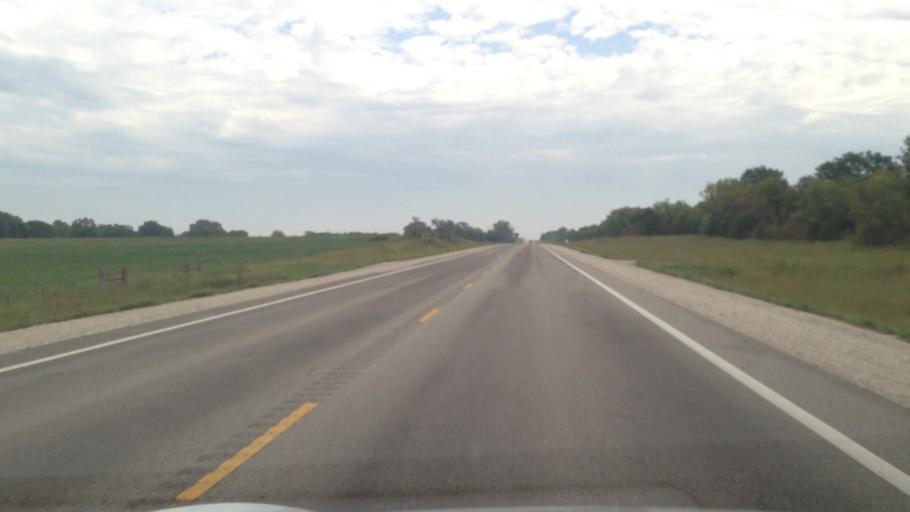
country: US
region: Kansas
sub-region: Allen County
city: Iola
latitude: 37.9107
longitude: -95.1250
